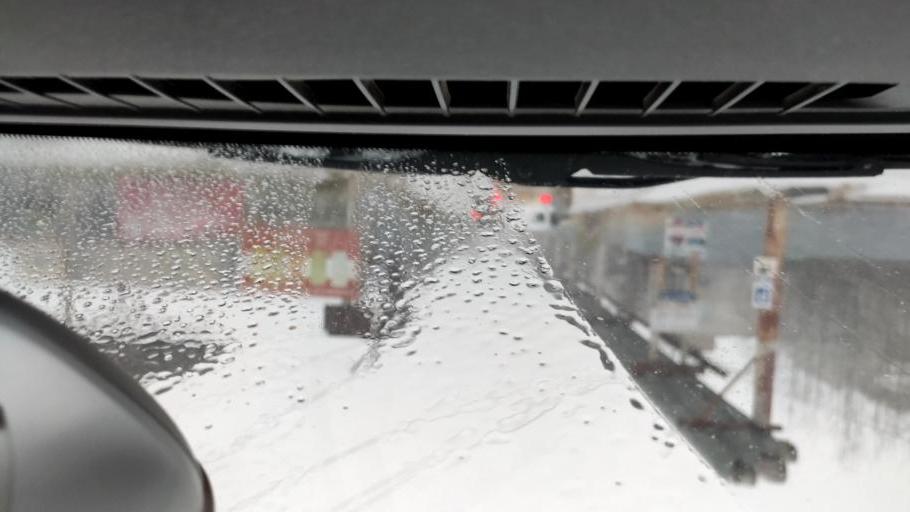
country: RU
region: Perm
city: Froly
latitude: 57.9616
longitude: 56.2730
